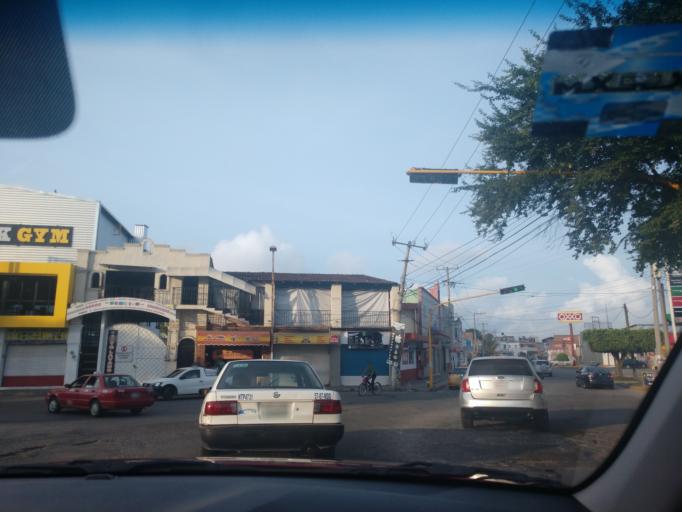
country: MX
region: Nayarit
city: Tepic
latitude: 21.5146
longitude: -104.8843
